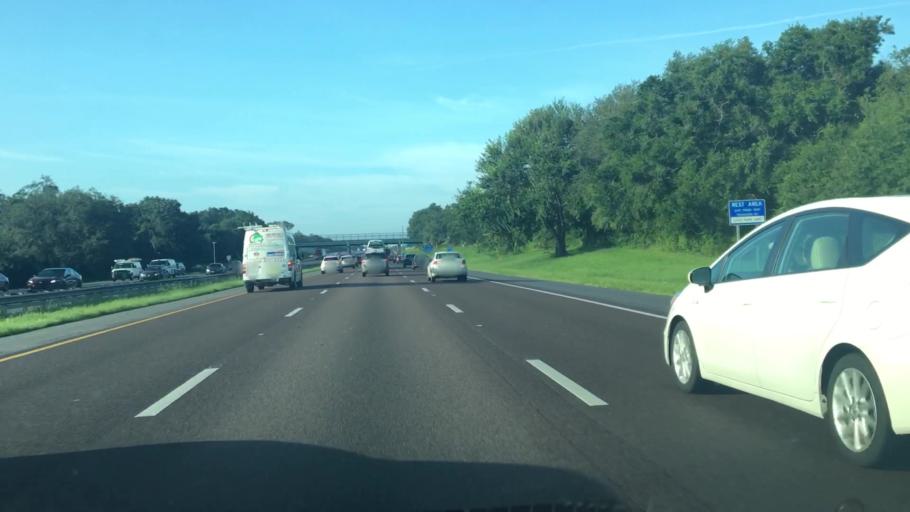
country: US
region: Florida
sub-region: Seminole County
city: Longwood
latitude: 28.7148
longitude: -81.3735
